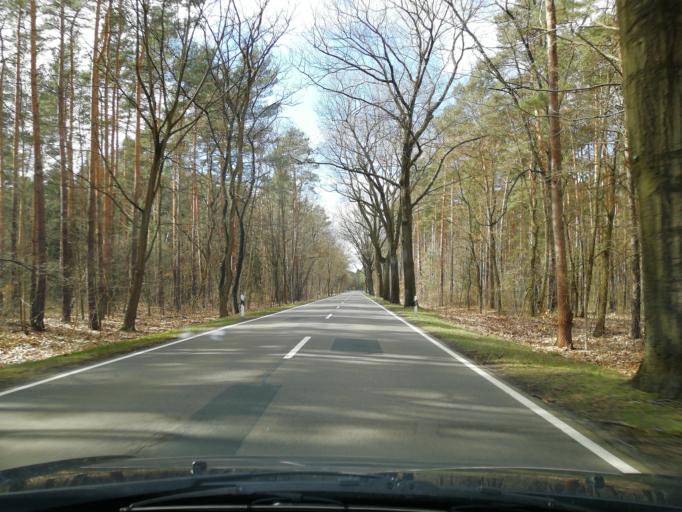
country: DE
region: Brandenburg
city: Altdobern
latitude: 51.7150
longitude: 14.0238
